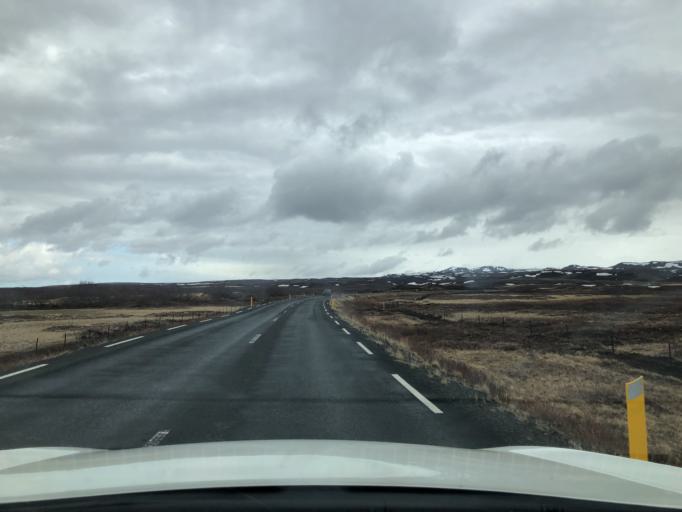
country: IS
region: Northeast
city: Laugar
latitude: 65.6436
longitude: -17.0003
